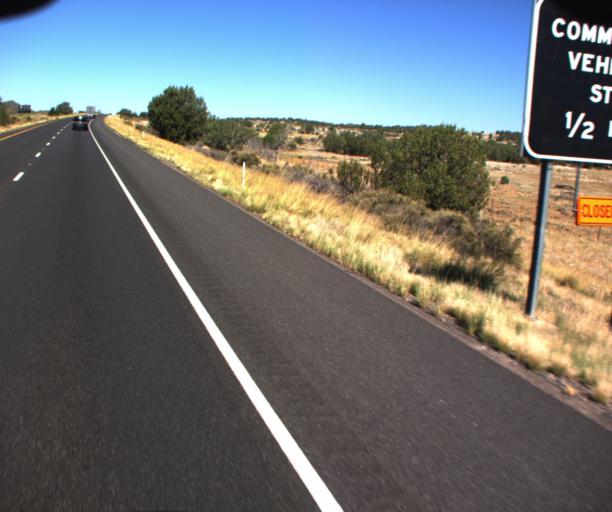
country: US
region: Arizona
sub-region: Yavapai County
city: Paulden
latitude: 35.2577
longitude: -112.7107
